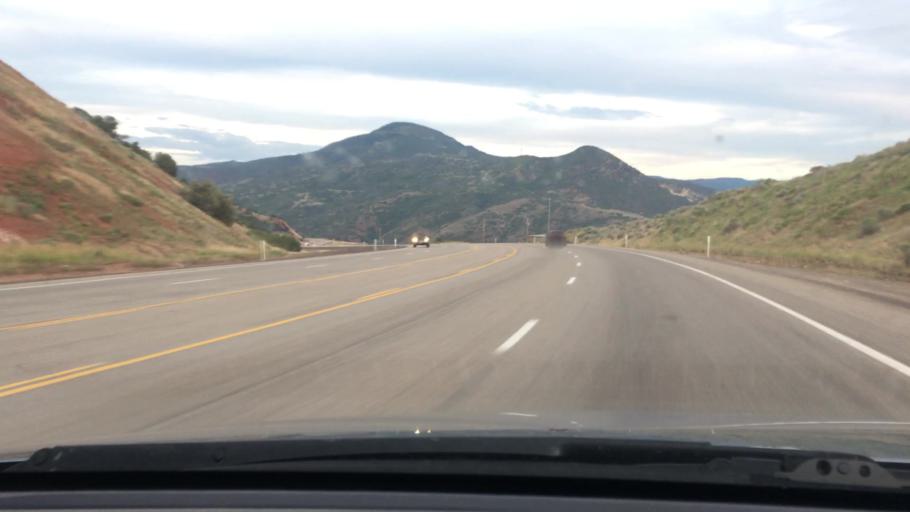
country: US
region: Utah
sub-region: Utah County
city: Mapleton
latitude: 40.0023
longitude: -111.4901
